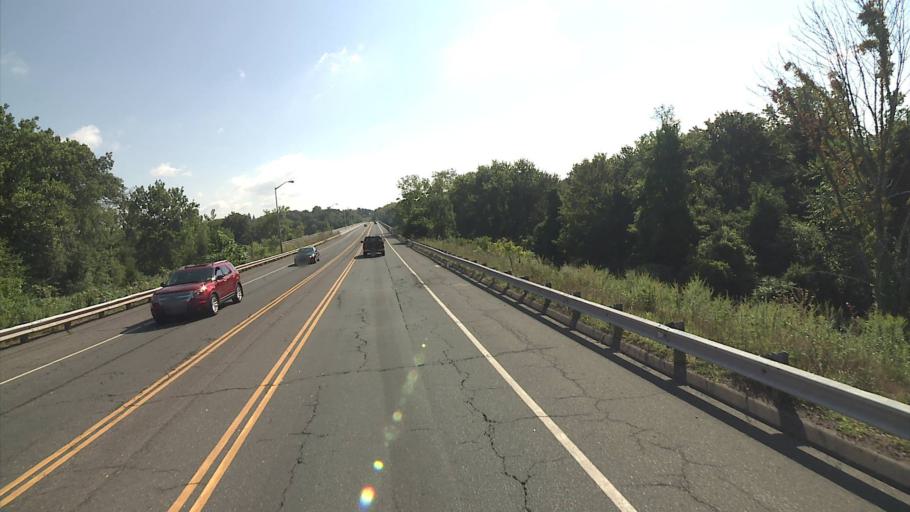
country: US
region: Connecticut
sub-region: Hartford County
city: Thompsonville
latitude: 41.9889
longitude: -72.6073
